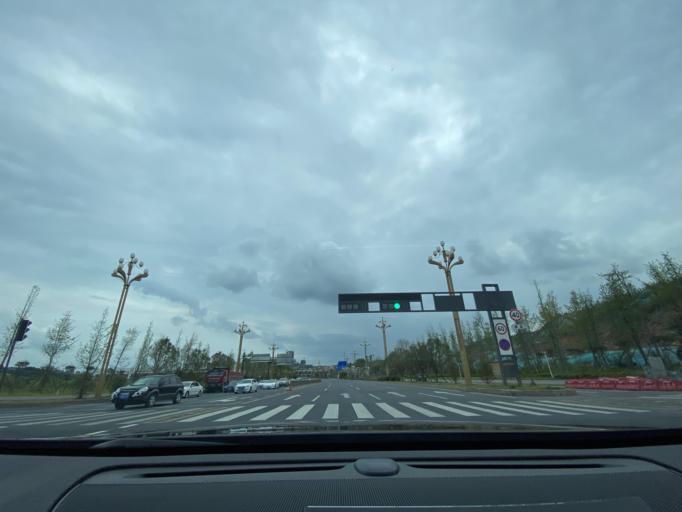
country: CN
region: Sichuan
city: Jiancheng
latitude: 30.4462
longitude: 104.4959
